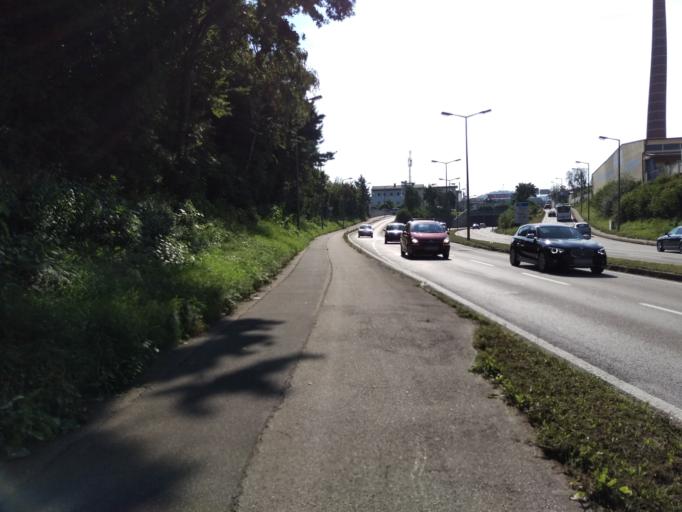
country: AT
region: Styria
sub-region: Politischer Bezirk Graz-Umgebung
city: Feldkirchen bei Graz
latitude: 47.0297
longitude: 15.4360
